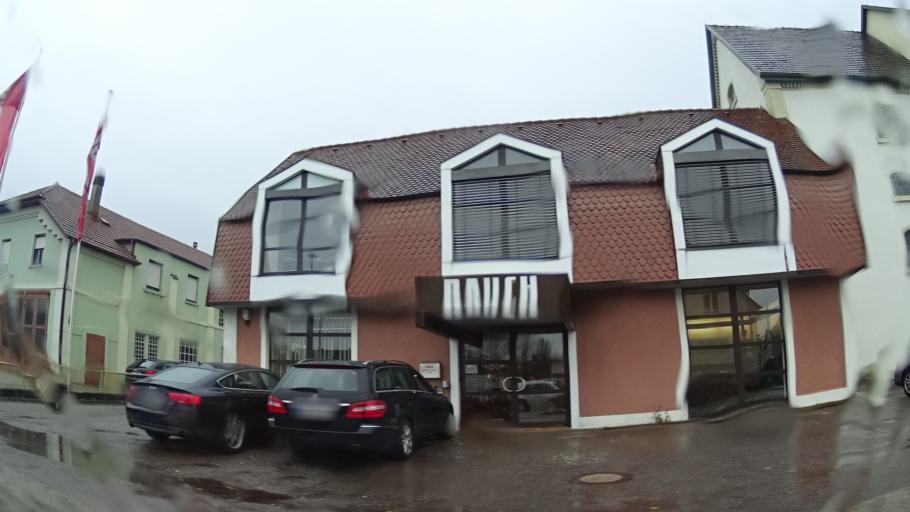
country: DE
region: Baden-Wuerttemberg
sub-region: Karlsruhe Region
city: Sinzheim
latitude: 48.7599
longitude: 8.1686
